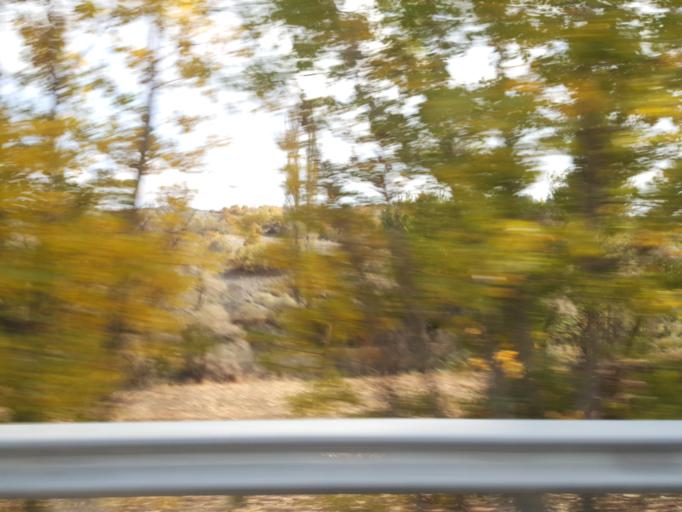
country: TR
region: Corum
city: Alaca
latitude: 40.3267
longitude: 34.7026
